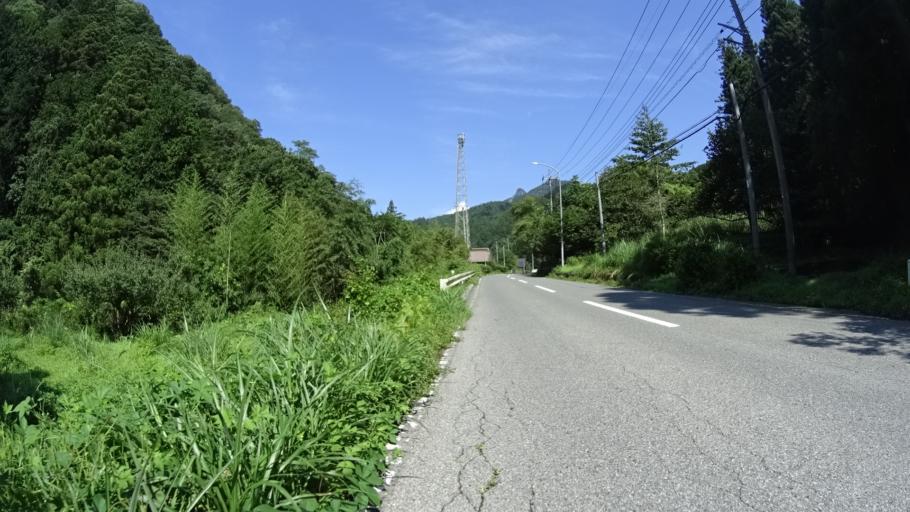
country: JP
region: Saitama
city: Chichibu
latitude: 36.0459
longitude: 138.8897
